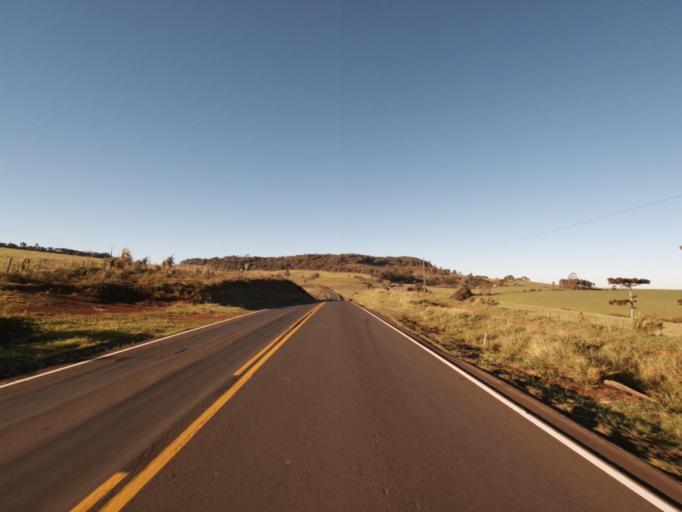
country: AR
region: Misiones
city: Bernardo de Irigoyen
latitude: -26.3499
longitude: -53.5450
